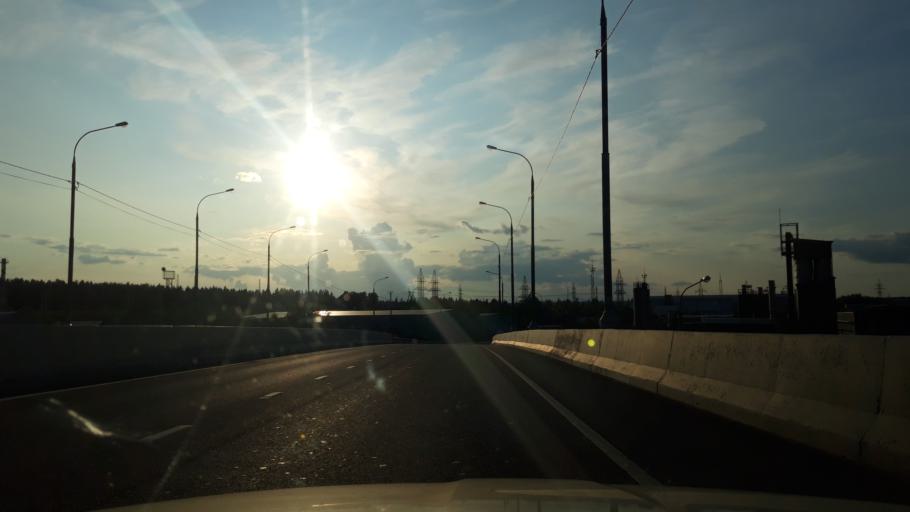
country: RU
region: Moscow
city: Zelenograd
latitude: 55.9949
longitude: 37.1612
